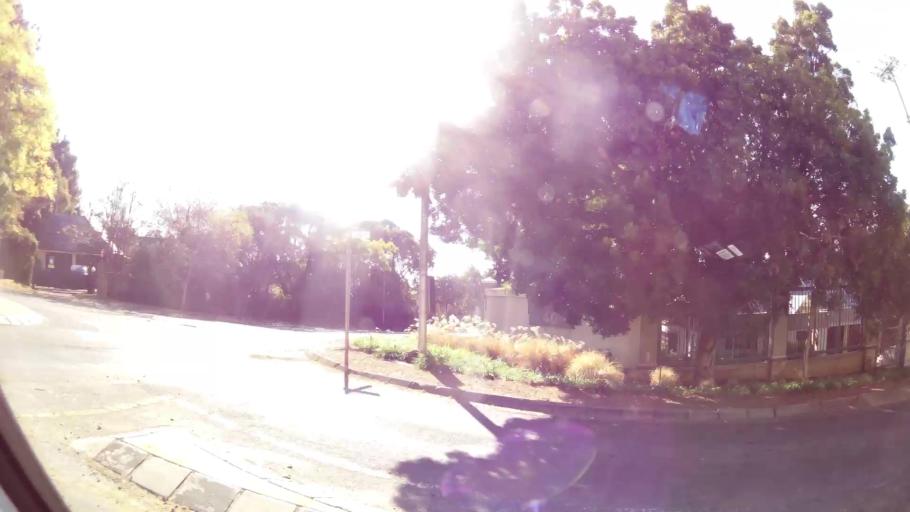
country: ZA
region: Gauteng
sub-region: City of Tshwane Metropolitan Municipality
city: Pretoria
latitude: -25.7875
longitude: 28.2578
